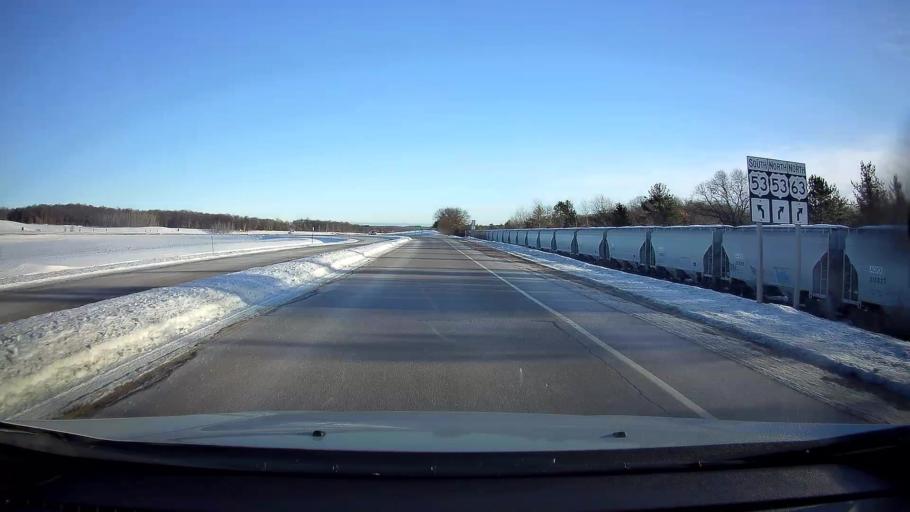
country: US
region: Wisconsin
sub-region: Washburn County
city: Spooner
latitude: 45.8529
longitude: -91.8579
